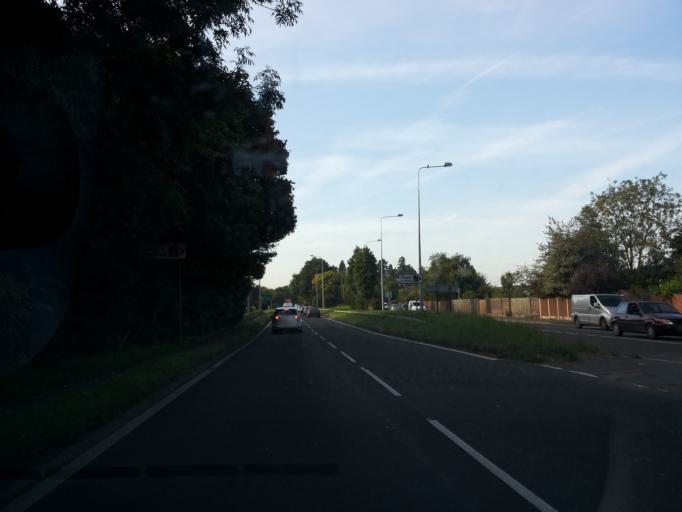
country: GB
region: England
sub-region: Staffordshire
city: Stone
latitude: 52.8875
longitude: -2.1375
